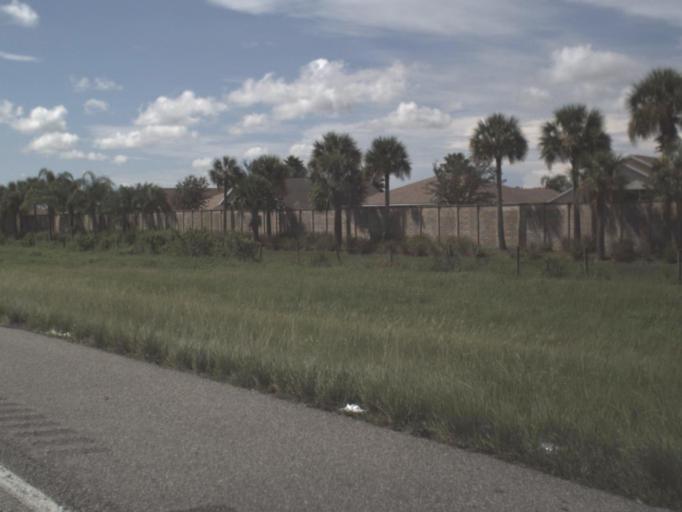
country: US
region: Florida
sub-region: Charlotte County
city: Harbour Heights
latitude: 27.0063
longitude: -82.0401
